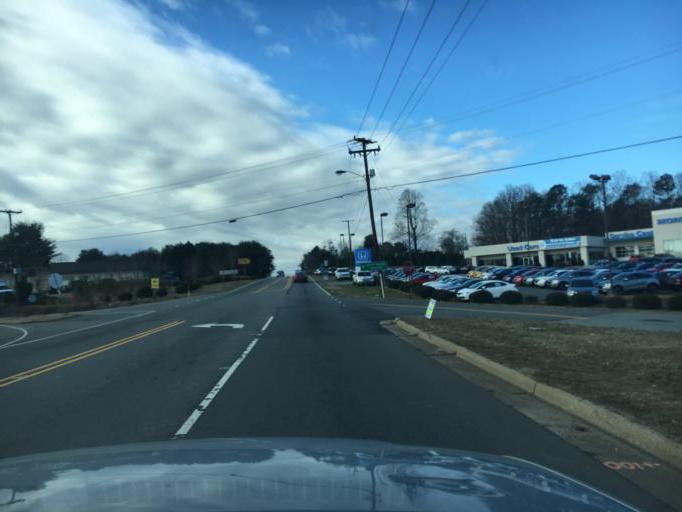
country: US
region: North Carolina
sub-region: Burke County
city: Salem
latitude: 35.7108
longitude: -81.7018
